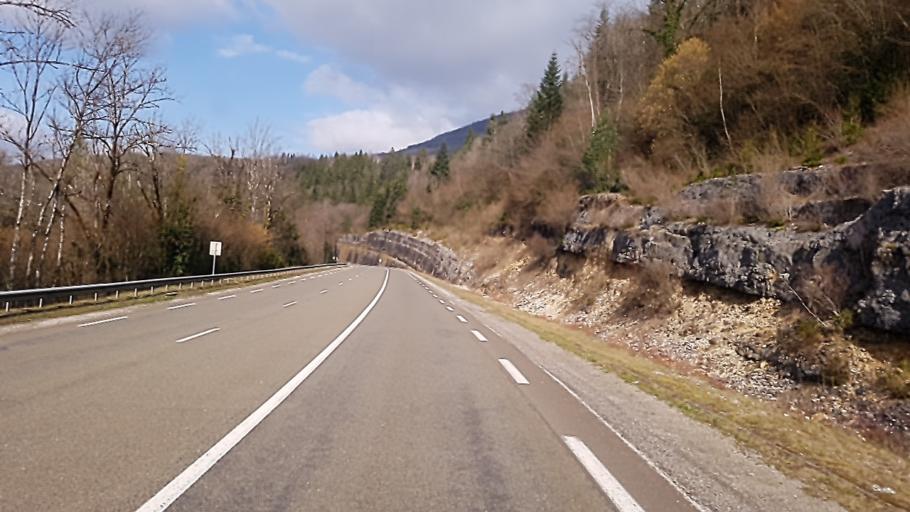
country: FR
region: Rhone-Alpes
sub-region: Departement de l'Ain
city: Dortan
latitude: 46.3366
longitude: 5.6876
